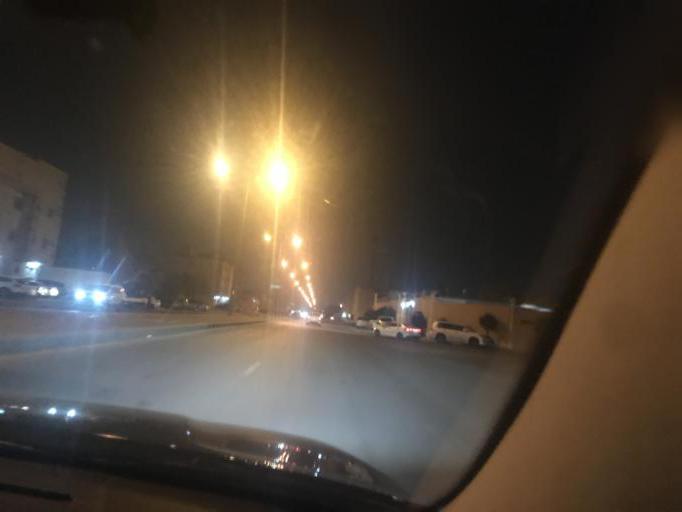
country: SA
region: Ar Riyad
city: Riyadh
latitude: 24.8237
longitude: 46.7403
